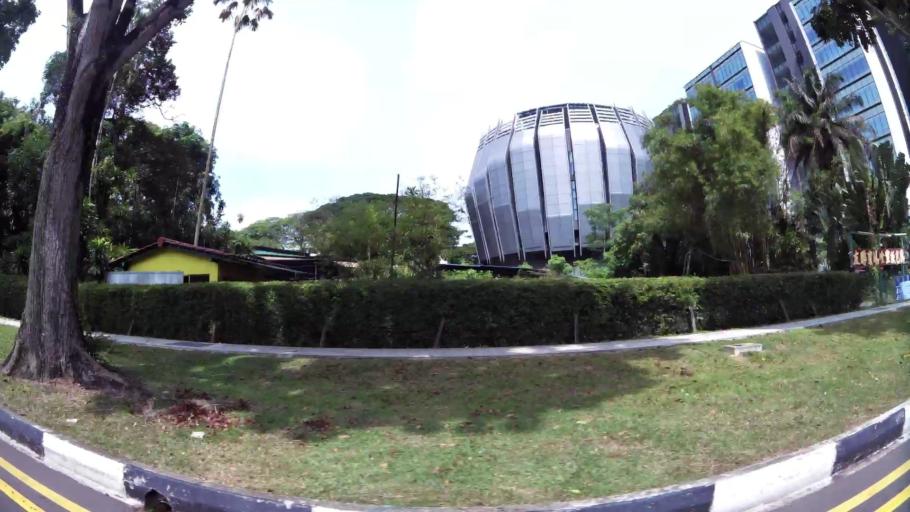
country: SG
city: Singapore
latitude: 1.3278
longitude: 103.7762
